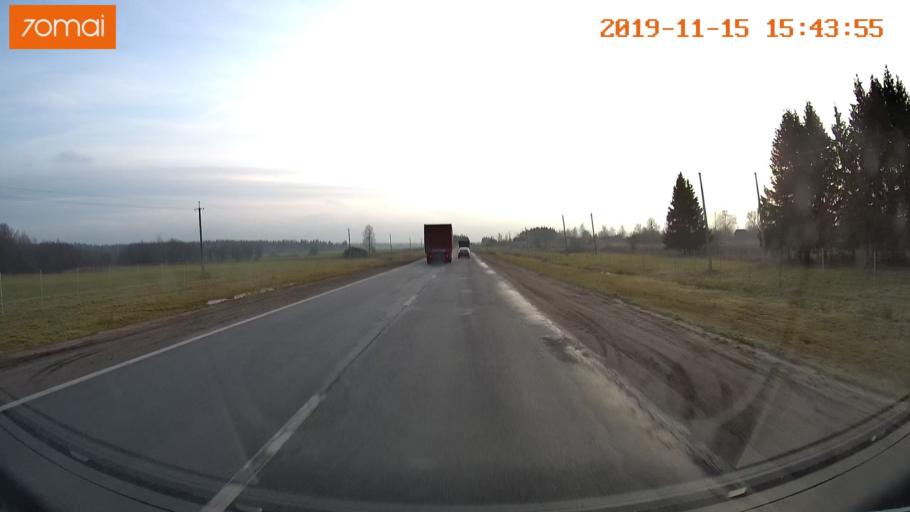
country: RU
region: Jaroslavl
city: Danilov
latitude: 57.9765
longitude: 40.0247
